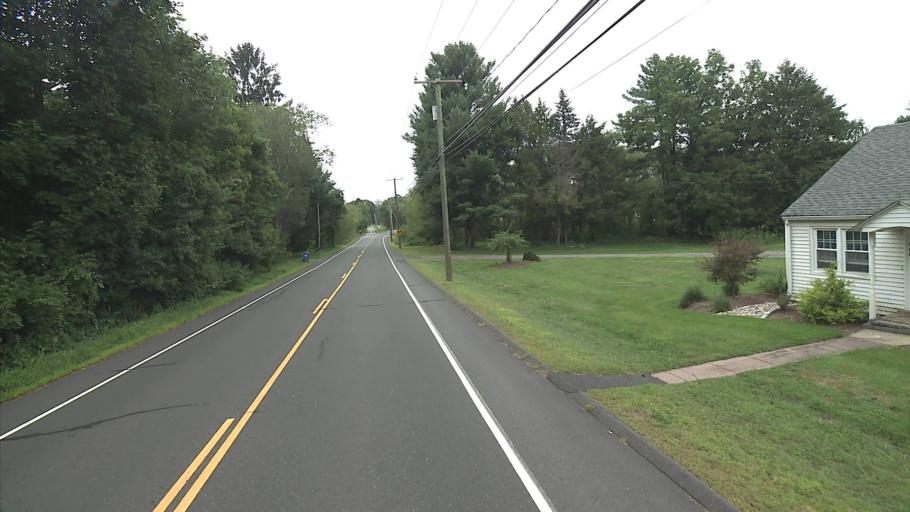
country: US
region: Connecticut
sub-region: Tolland County
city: Tolland
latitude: 41.8793
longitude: -72.3514
